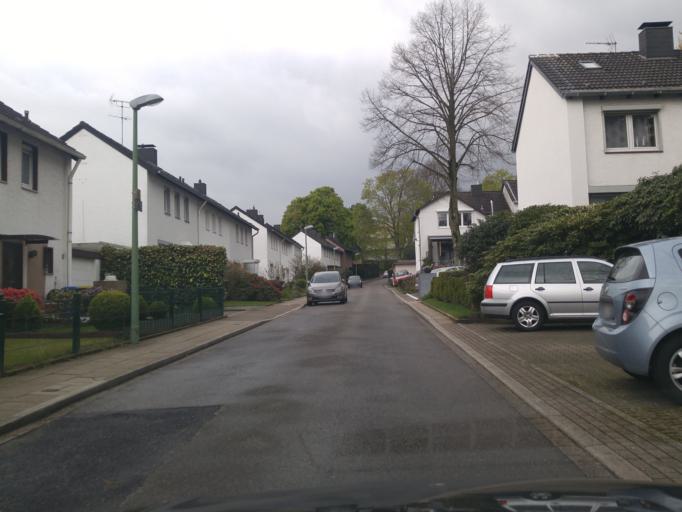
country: DE
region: North Rhine-Westphalia
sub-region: Regierungsbezirk Dusseldorf
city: Essen
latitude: 51.4321
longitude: 7.0321
